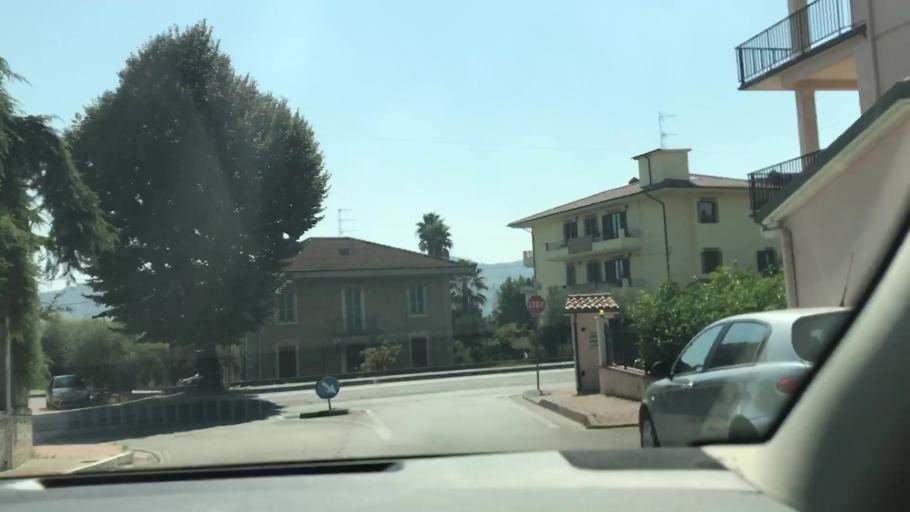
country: IT
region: The Marches
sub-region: Provincia di Ascoli Piceno
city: San Benedetto del Tronto
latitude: 42.9073
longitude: 13.8733
